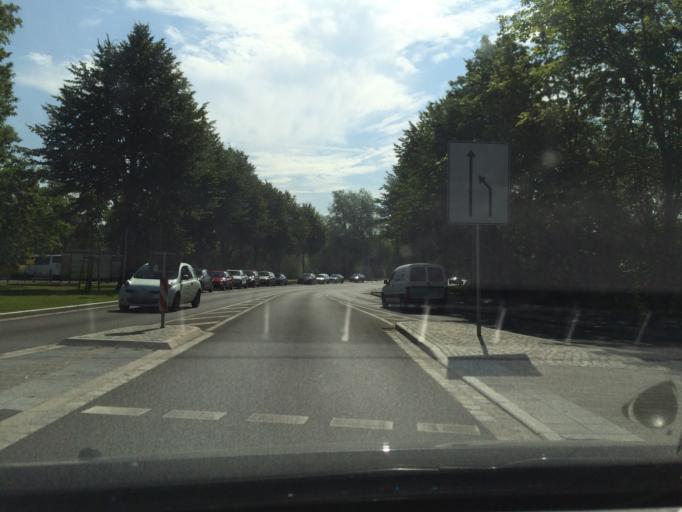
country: DE
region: Mecklenburg-Vorpommern
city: Stralsund
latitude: 54.3081
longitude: 13.0871
